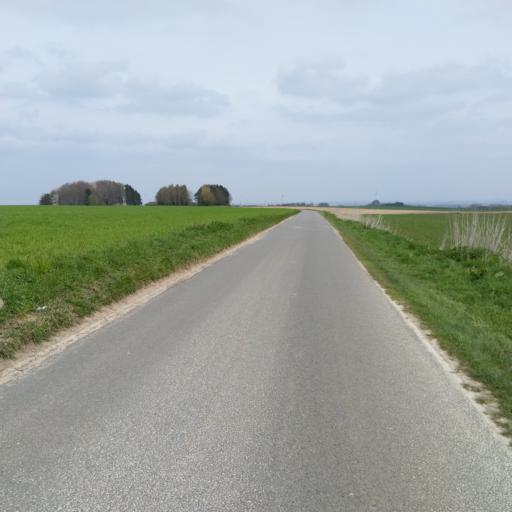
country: BE
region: Wallonia
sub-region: Province du Hainaut
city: Quevy-le-Petit
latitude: 50.3430
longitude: 3.9304
